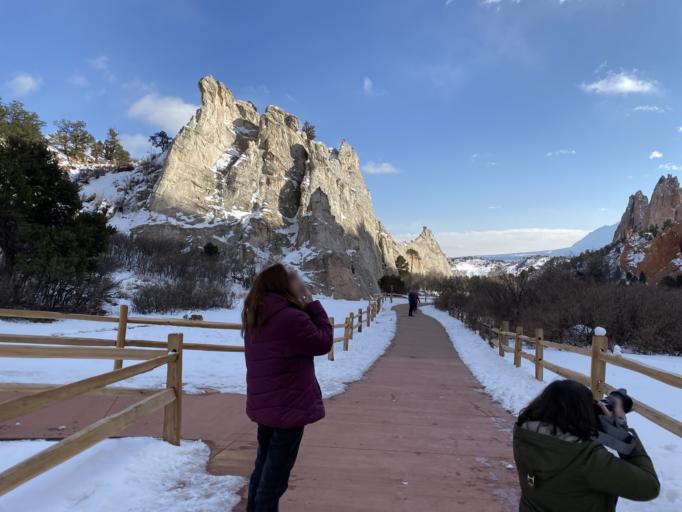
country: US
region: Colorado
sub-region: El Paso County
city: Manitou Springs
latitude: 38.8807
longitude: -104.8801
